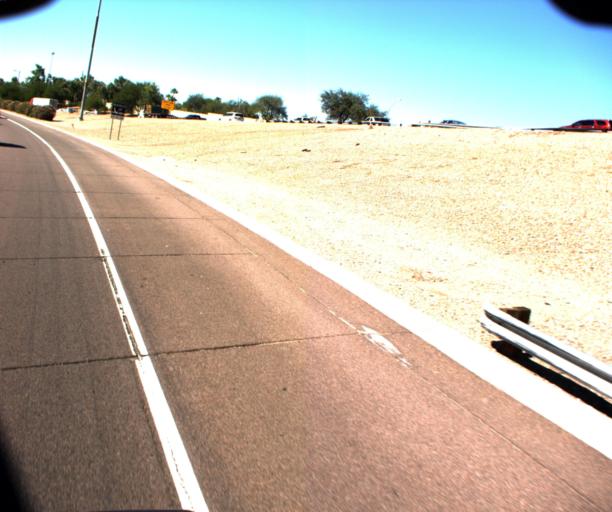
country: US
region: Arizona
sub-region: Maricopa County
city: Phoenix
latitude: 33.4621
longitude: -112.0401
